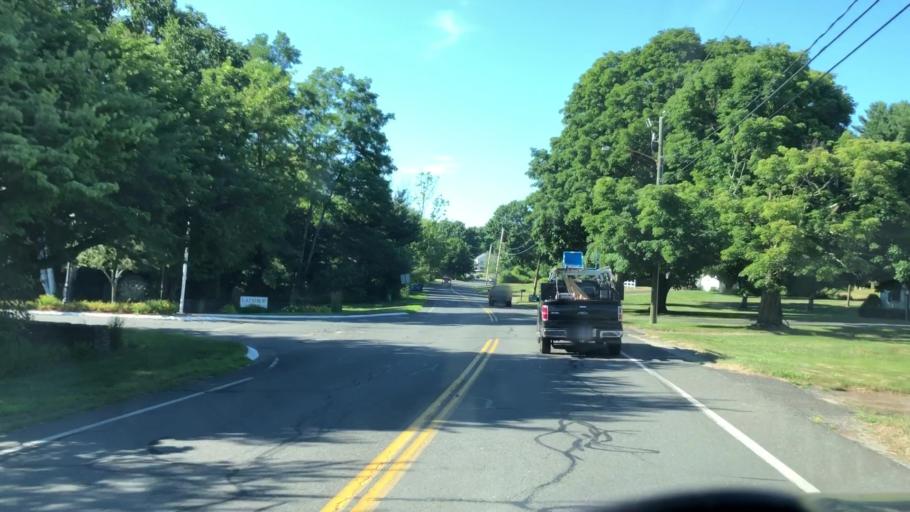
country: US
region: Massachusetts
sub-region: Hampshire County
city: Easthampton
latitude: 42.2896
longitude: -72.6721
